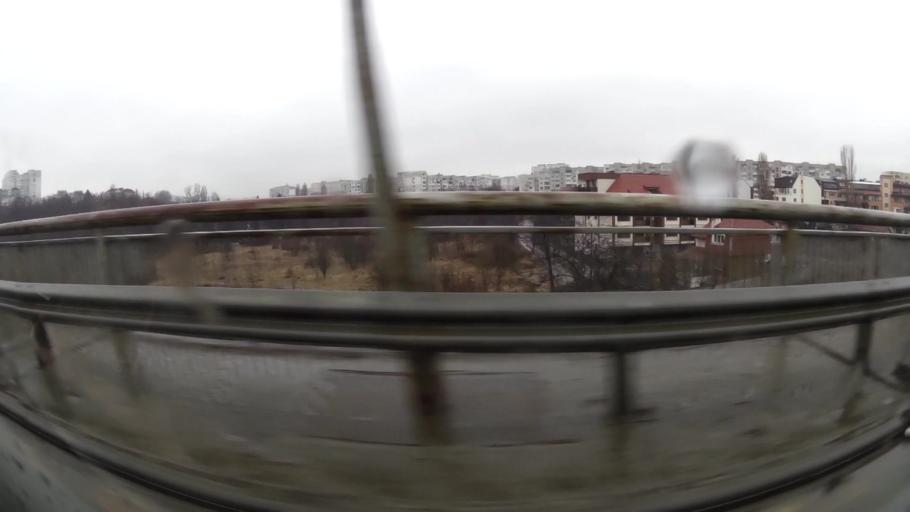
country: BG
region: Sofia-Capital
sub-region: Stolichna Obshtina
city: Sofia
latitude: 42.6571
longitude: 23.3668
